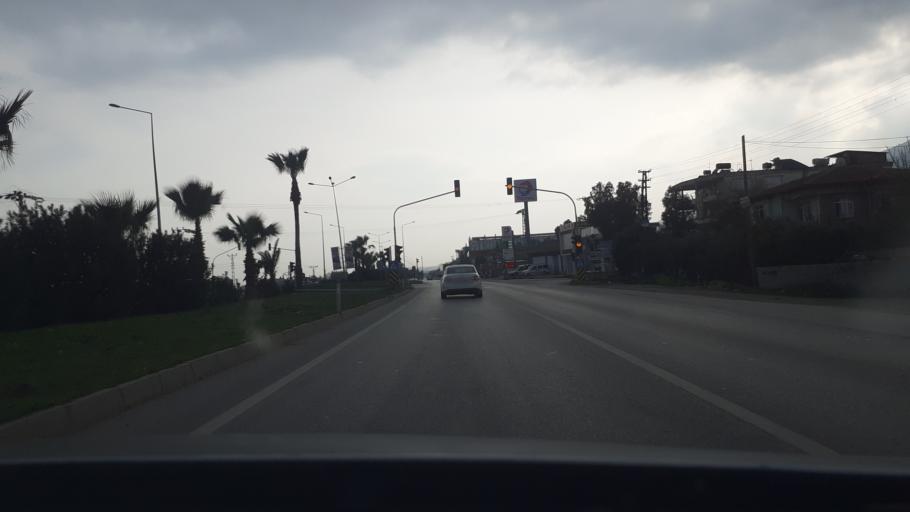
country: TR
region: Hatay
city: Serinyol
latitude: 36.3591
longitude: 36.2198
